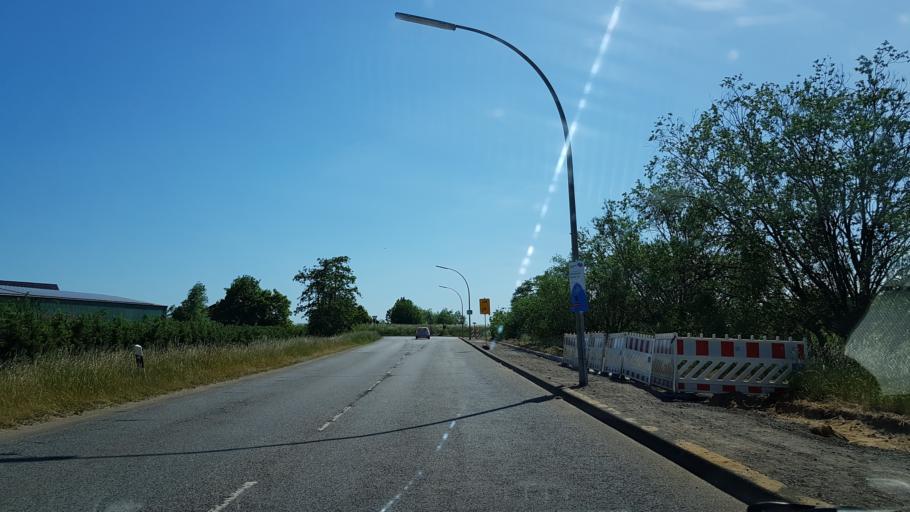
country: DE
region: Lower Saxony
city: Neu Wulmstorf
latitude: 53.5277
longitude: 9.8019
